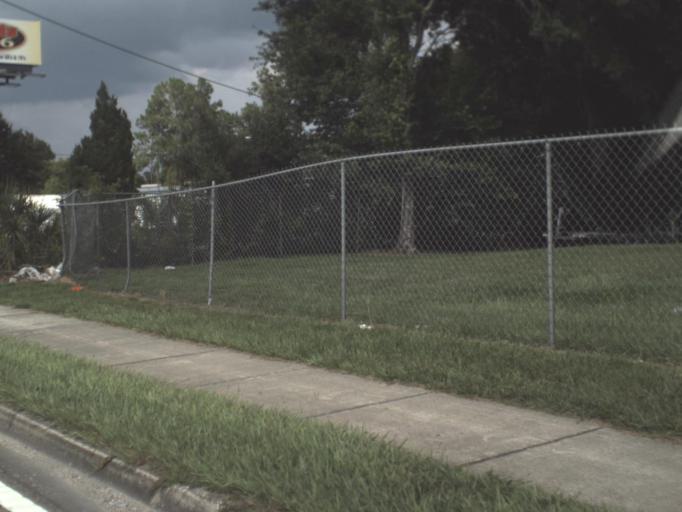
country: US
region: Florida
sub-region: Pasco County
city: Land O' Lakes
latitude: 28.2113
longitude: -82.4614
